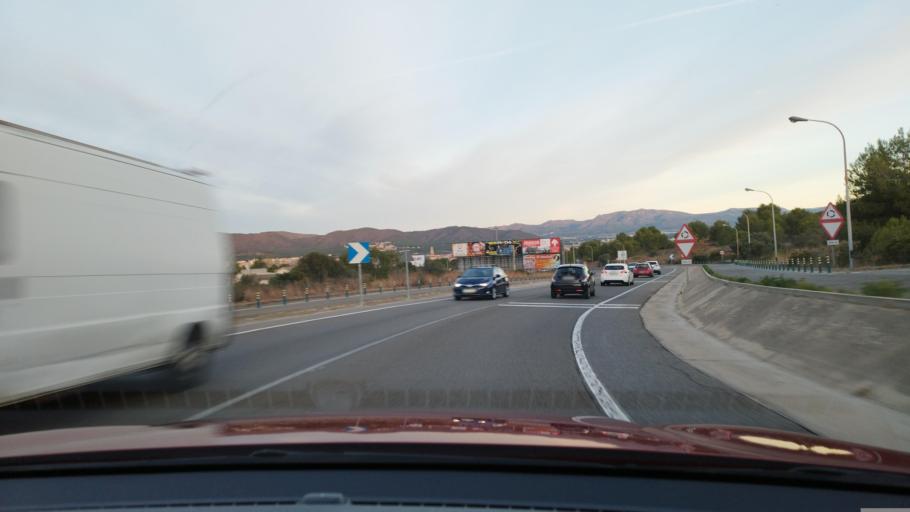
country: ES
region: Catalonia
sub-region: Provincia de Tarragona
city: El Vendrell
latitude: 41.2086
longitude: 1.5503
